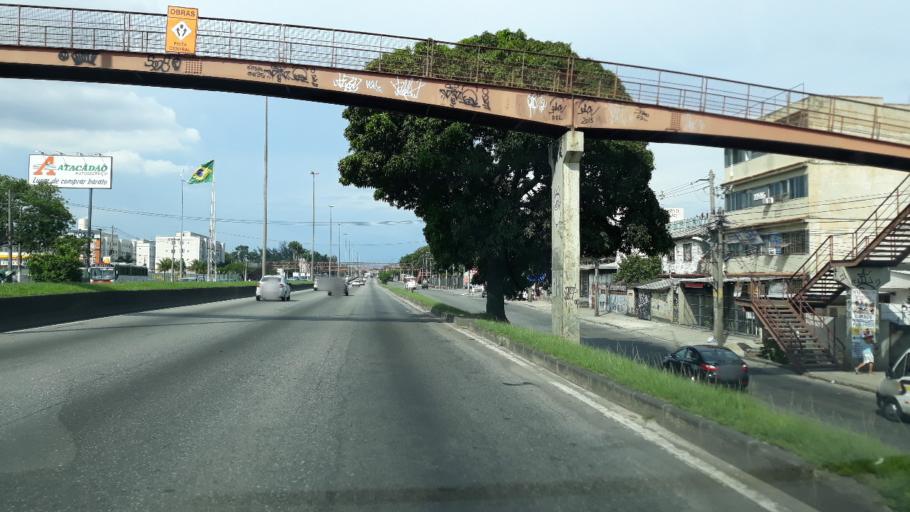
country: BR
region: Rio de Janeiro
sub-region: Sao Joao De Meriti
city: Sao Joao de Meriti
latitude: -22.8444
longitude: -43.3761
